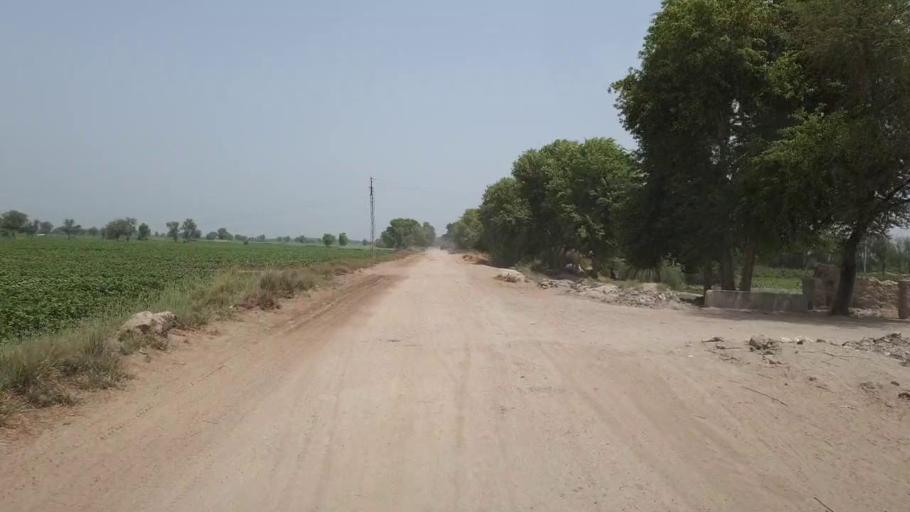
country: PK
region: Sindh
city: Nawabshah
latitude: 26.3236
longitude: 68.2969
